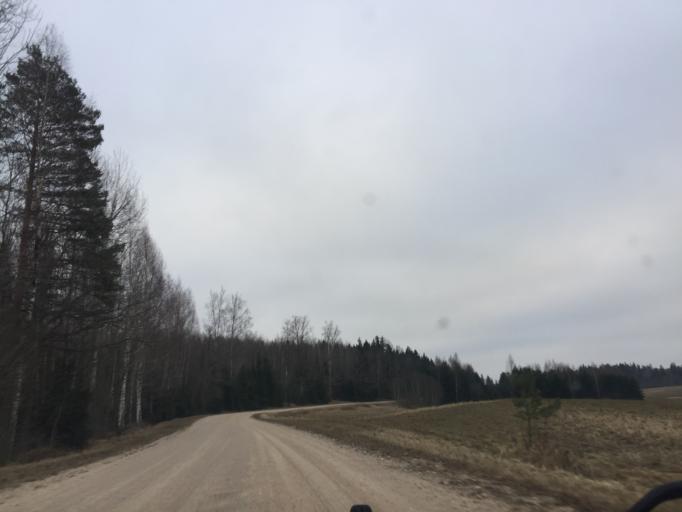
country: LV
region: Ligatne
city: Ligatne
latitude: 57.2169
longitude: 25.1293
